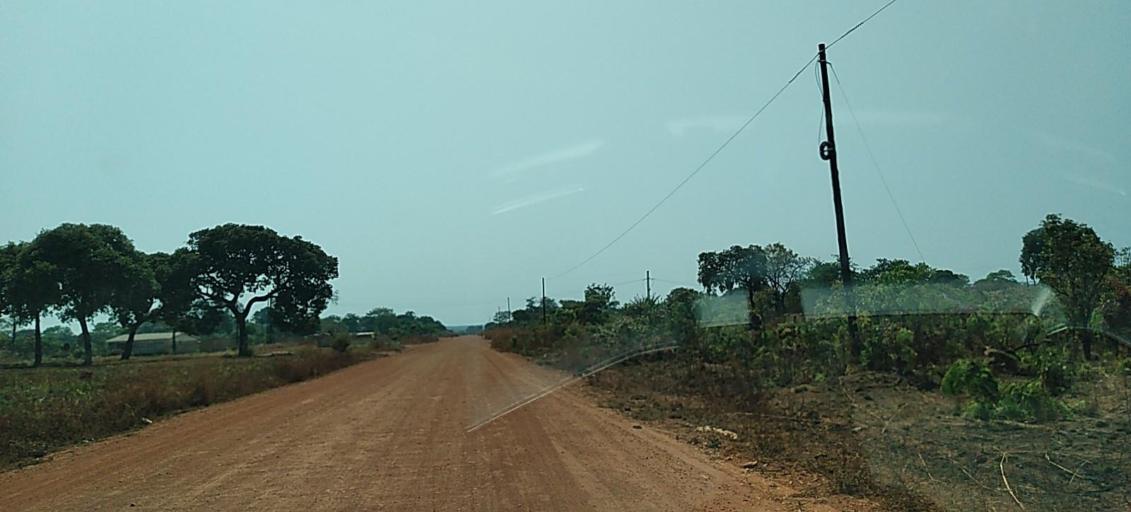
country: ZM
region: North-Western
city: Kansanshi
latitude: -11.9970
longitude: 26.6044
